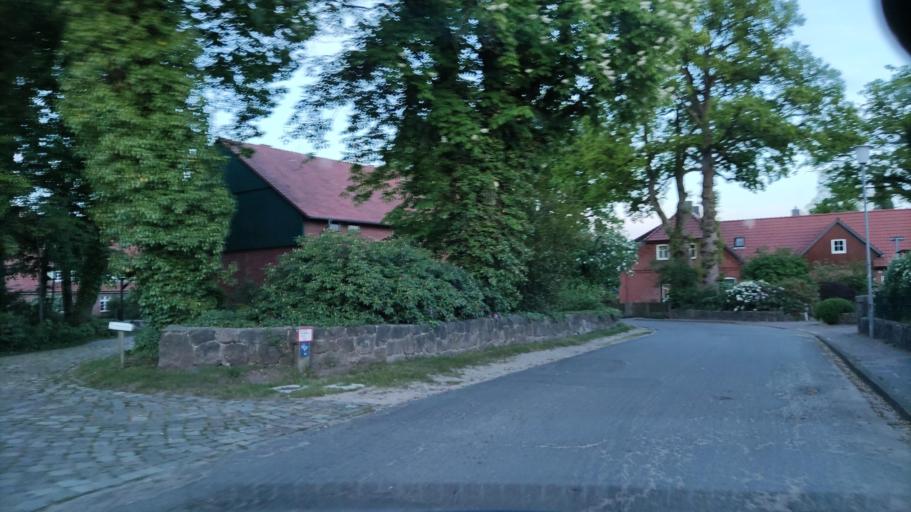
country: DE
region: Lower Saxony
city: Egestorf
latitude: 53.1945
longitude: 10.0616
